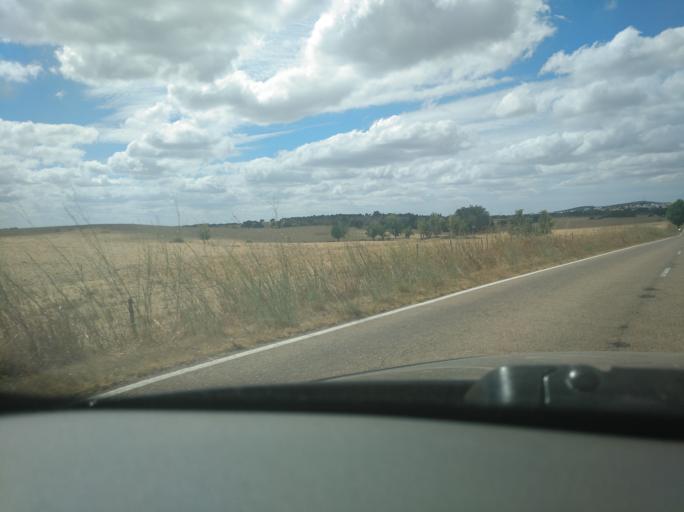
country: PT
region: Portalegre
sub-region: Arronches
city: Arronches
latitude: 39.0397
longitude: -7.4204
